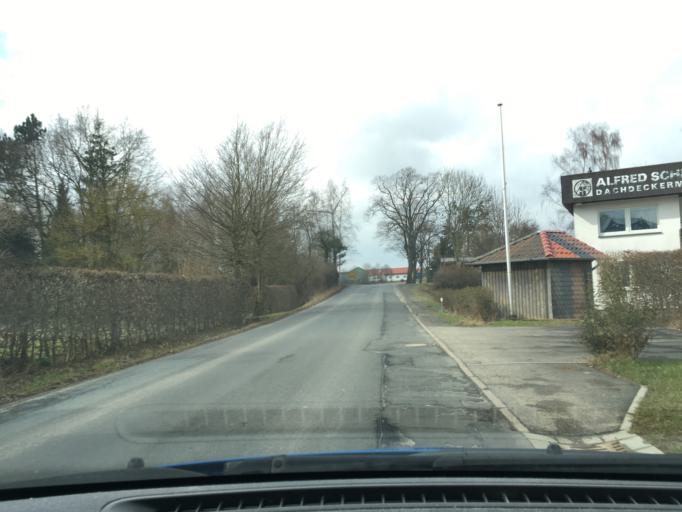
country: DE
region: Lower Saxony
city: Dransfeld
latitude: 51.5036
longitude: 9.7545
